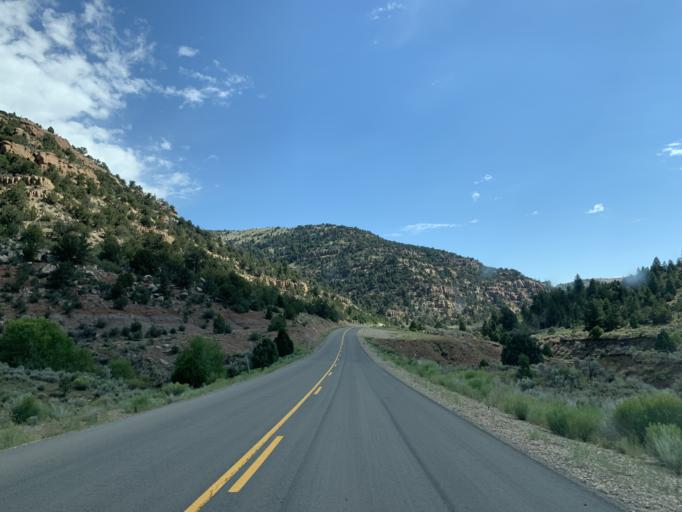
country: US
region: Utah
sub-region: Carbon County
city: East Carbon City
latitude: 39.7503
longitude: -110.5482
